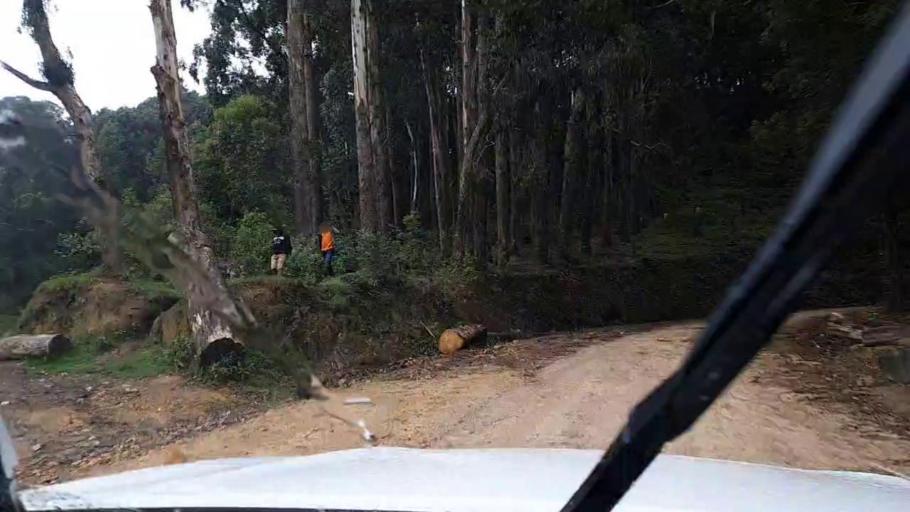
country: RW
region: Southern Province
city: Nzega
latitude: -2.3662
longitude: 29.3779
